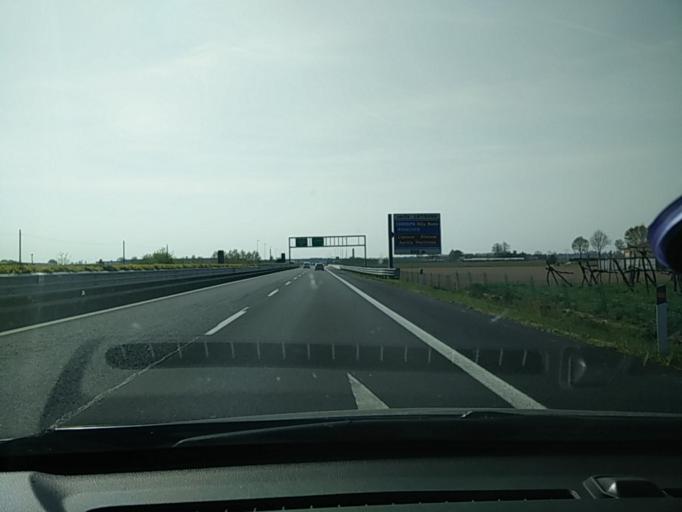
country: IT
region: Friuli Venezia Giulia
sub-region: Provincia di Udine
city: Ronchis
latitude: 45.8185
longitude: 13.0268
